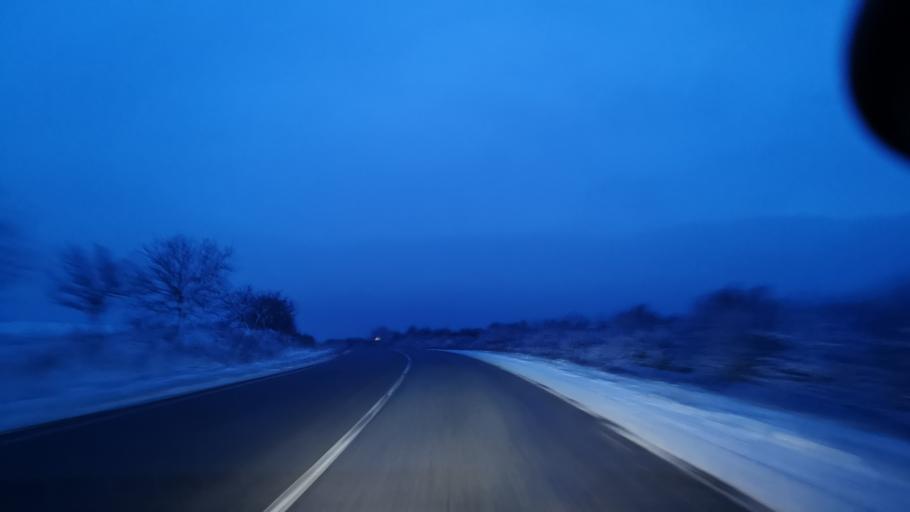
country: MD
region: Orhei
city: Orhei
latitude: 47.5561
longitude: 28.7966
